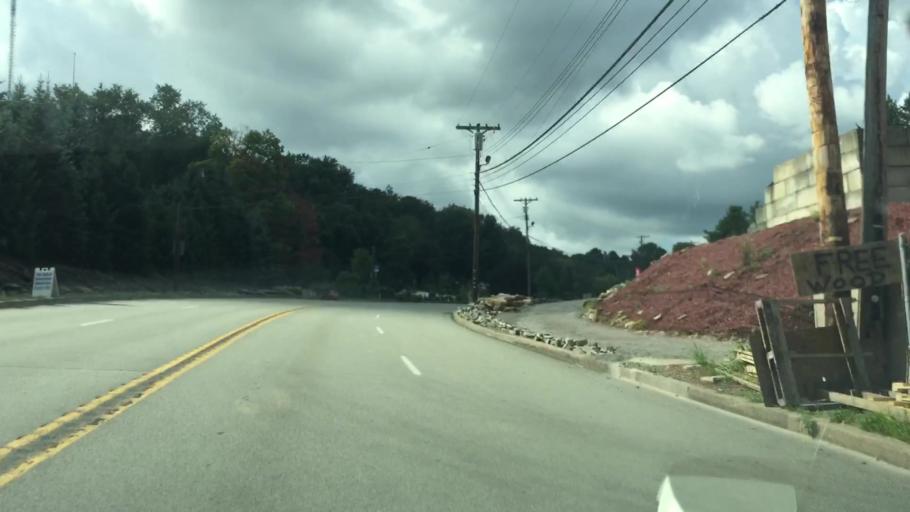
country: US
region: Pennsylvania
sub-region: Allegheny County
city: Millvale
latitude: 40.5016
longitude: -80.0031
